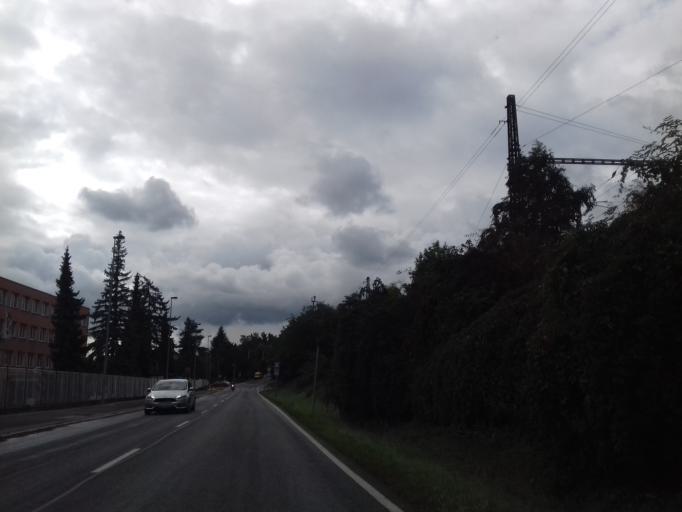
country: CZ
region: Praha
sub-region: Praha 12
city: Modrany
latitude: 49.9891
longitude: 14.3689
